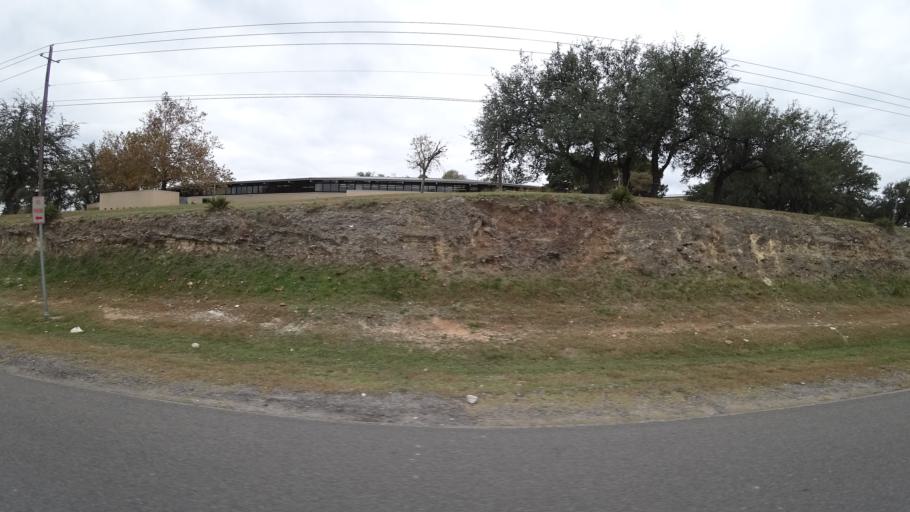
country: US
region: Texas
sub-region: Travis County
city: The Hills
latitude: 30.3292
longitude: -97.9658
